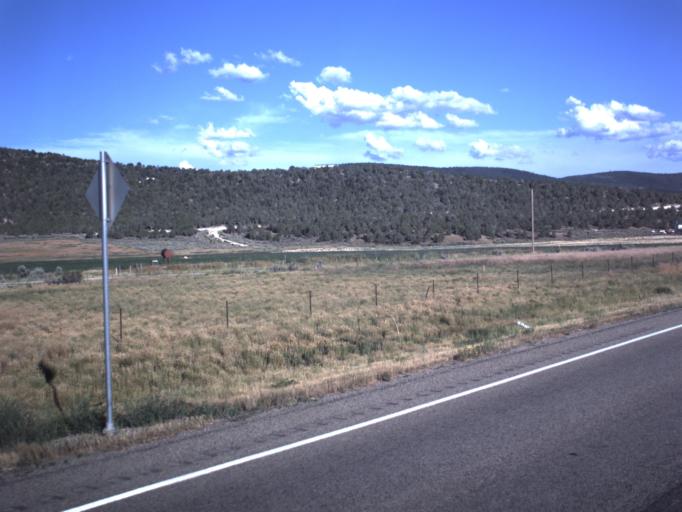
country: US
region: Utah
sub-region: Sanpete County
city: Fairview
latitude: 39.7763
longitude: -111.4900
